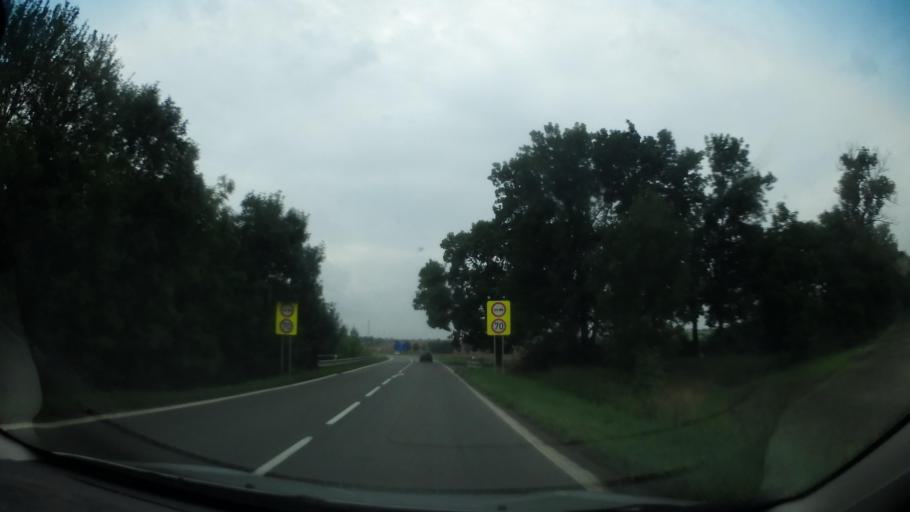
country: CZ
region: Olomoucky
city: Kojetin
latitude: 49.3321
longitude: 17.3154
